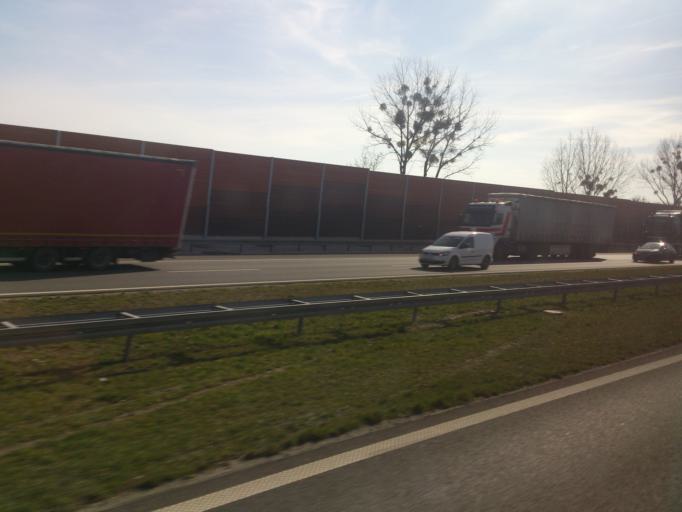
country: PL
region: Kujawsko-Pomorskie
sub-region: Powiat aleksandrowski
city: Waganiec
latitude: 52.8003
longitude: 18.8258
